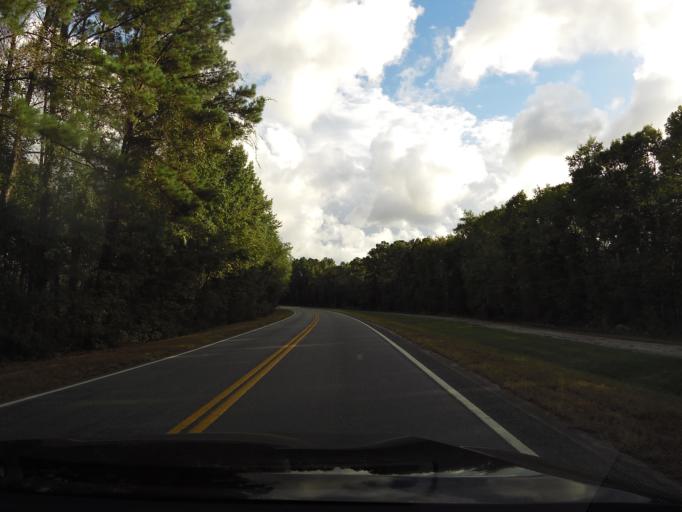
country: US
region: Georgia
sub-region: Liberty County
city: Midway
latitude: 31.7096
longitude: -81.4169
